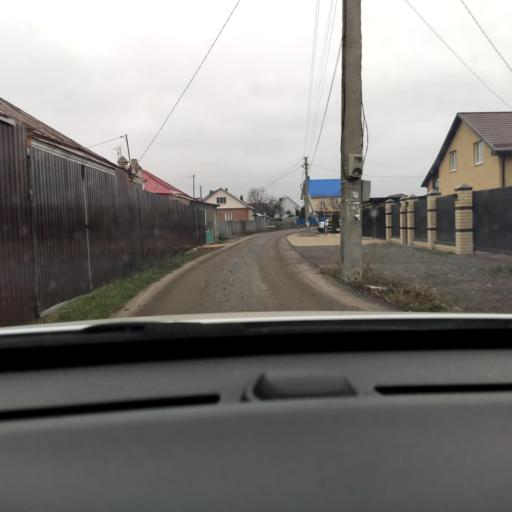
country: RU
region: Voronezj
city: Somovo
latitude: 51.6863
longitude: 39.3575
